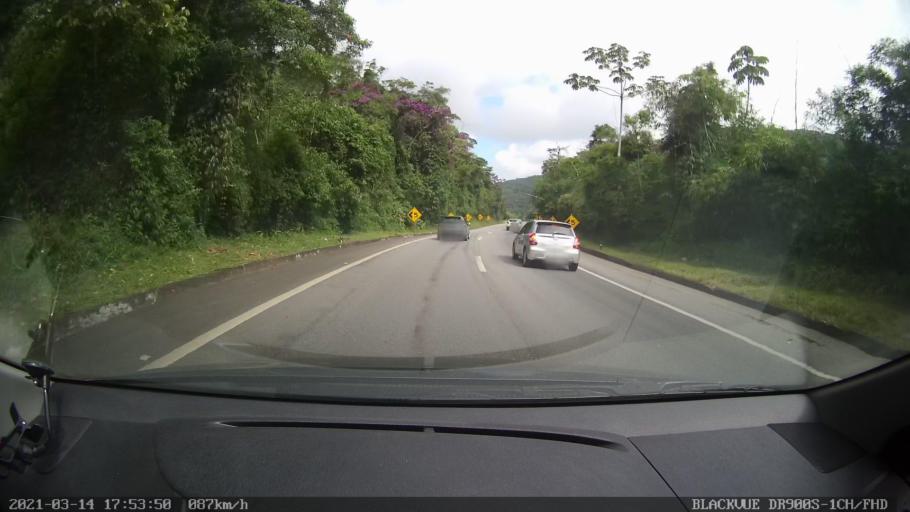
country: BR
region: Rio de Janeiro
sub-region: Petropolis
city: Petropolis
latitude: -22.4828
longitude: -43.2317
